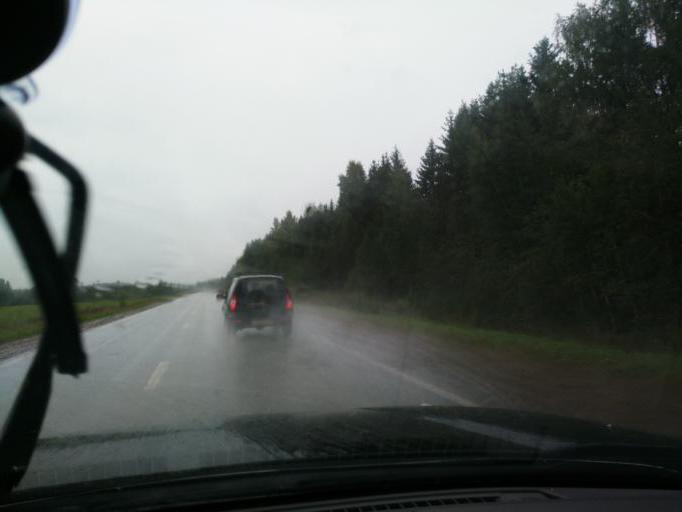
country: RU
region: Perm
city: Osa
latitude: 57.3464
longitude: 55.5923
